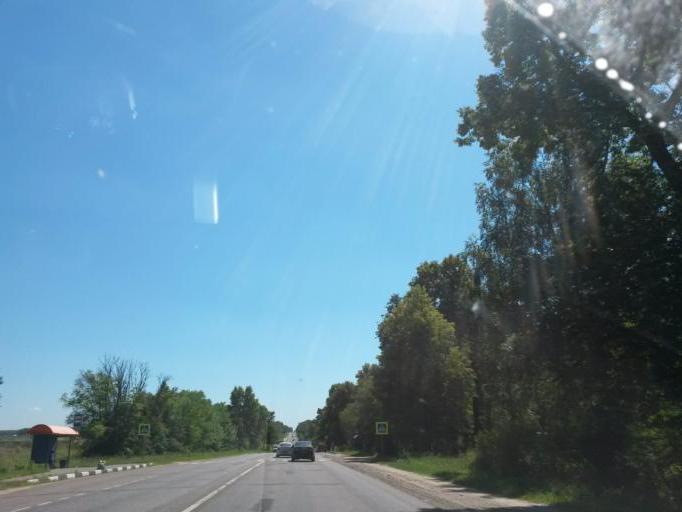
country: RU
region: Moskovskaya
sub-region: Chekhovskiy Rayon
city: Chekhov
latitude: 55.1030
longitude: 37.4452
